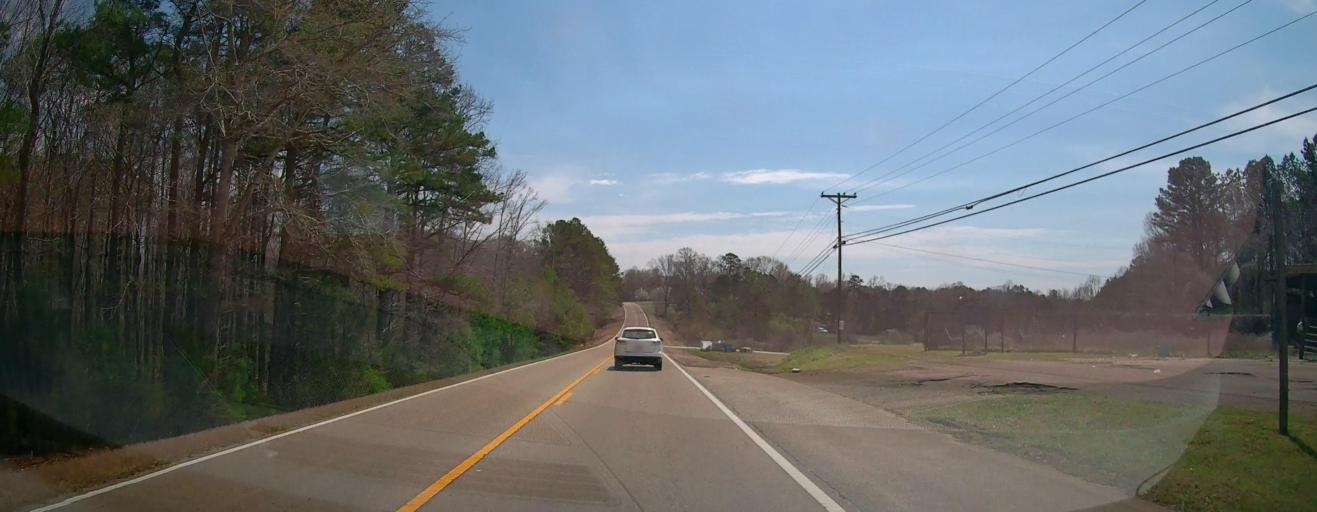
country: US
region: Mississippi
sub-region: Union County
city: New Albany
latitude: 34.4520
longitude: -88.9719
